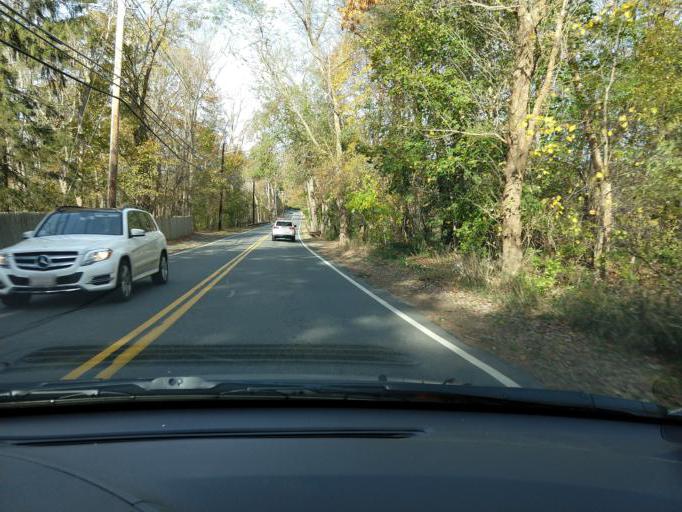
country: US
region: Massachusetts
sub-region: Middlesex County
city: Concord
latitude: 42.4705
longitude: -71.3615
